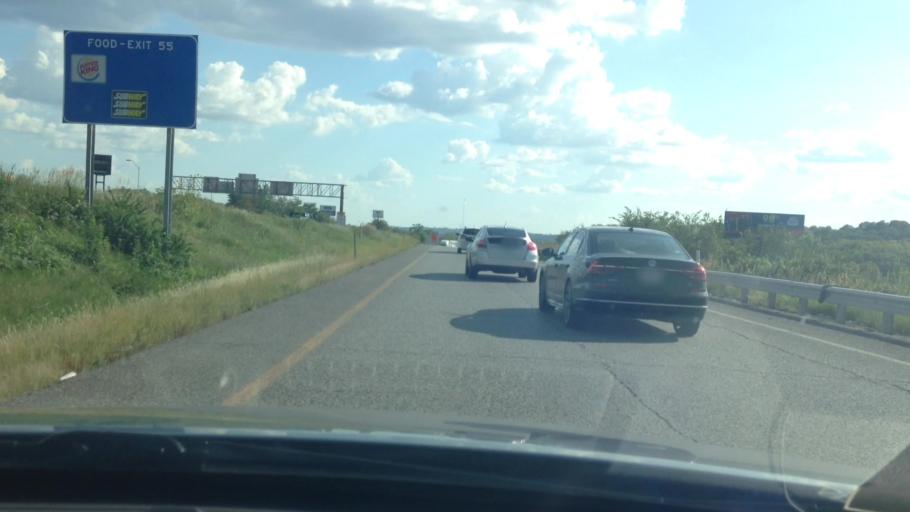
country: US
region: Missouri
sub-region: Clay County
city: Claycomo
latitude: 39.1674
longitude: -94.4941
